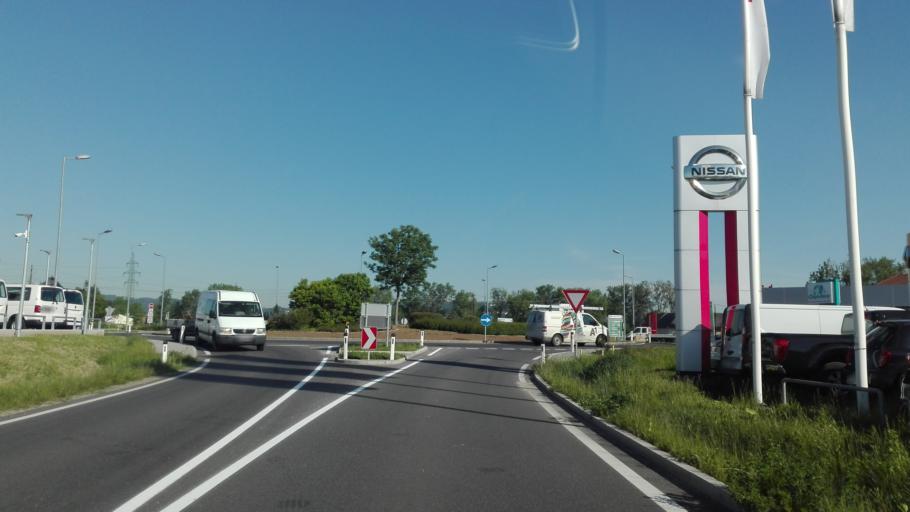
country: AT
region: Upper Austria
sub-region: Politischer Bezirk Urfahr-Umgebung
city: Feldkirchen an der Donau
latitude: 48.2994
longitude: 14.0143
